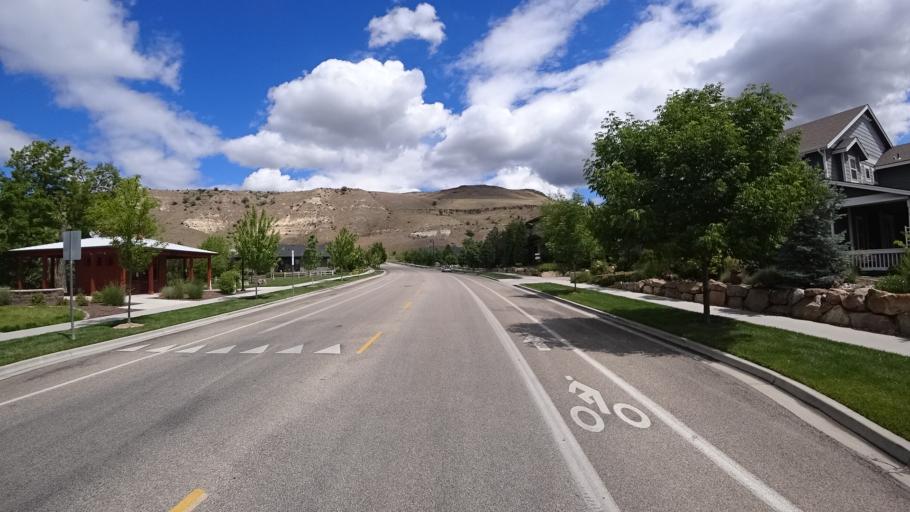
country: US
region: Idaho
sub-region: Ada County
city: Boise
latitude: 43.5782
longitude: -116.1387
